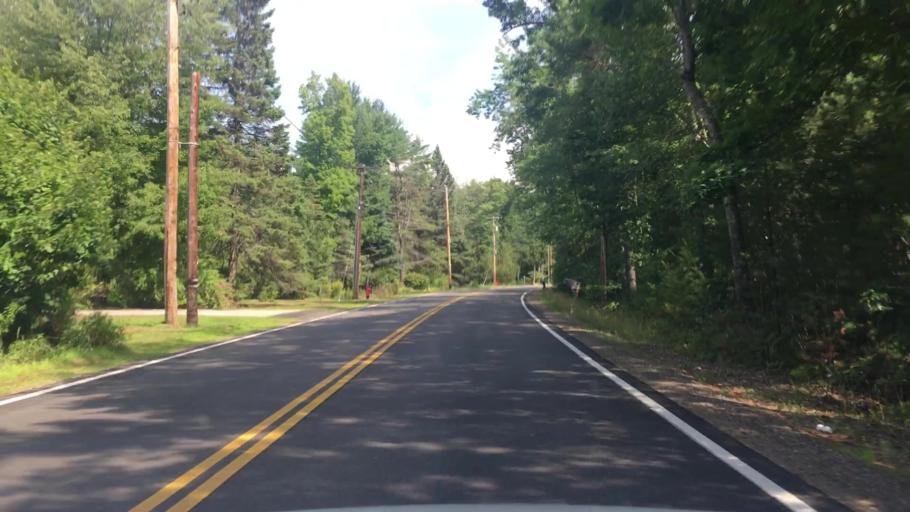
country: US
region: New Hampshire
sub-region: Strafford County
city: Rochester
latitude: 43.3390
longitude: -70.9612
